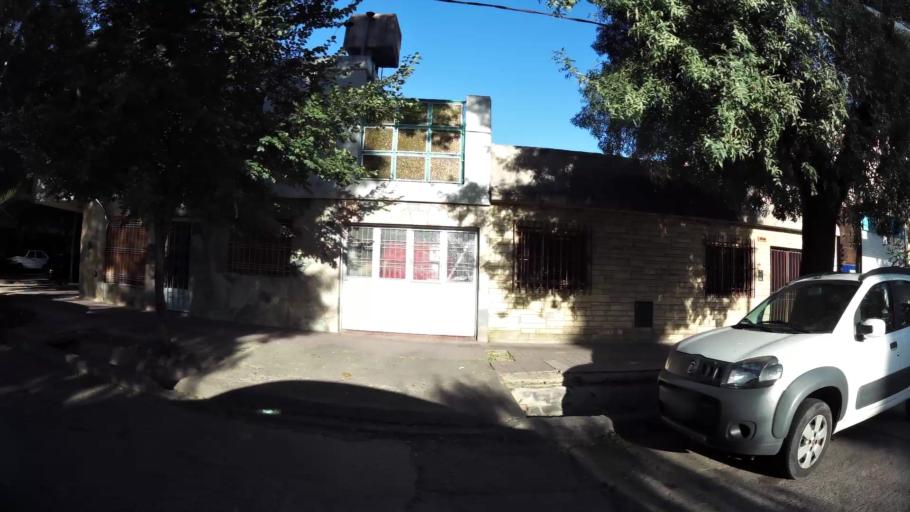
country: AR
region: Mendoza
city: Las Heras
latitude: -32.8698
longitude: -68.8292
